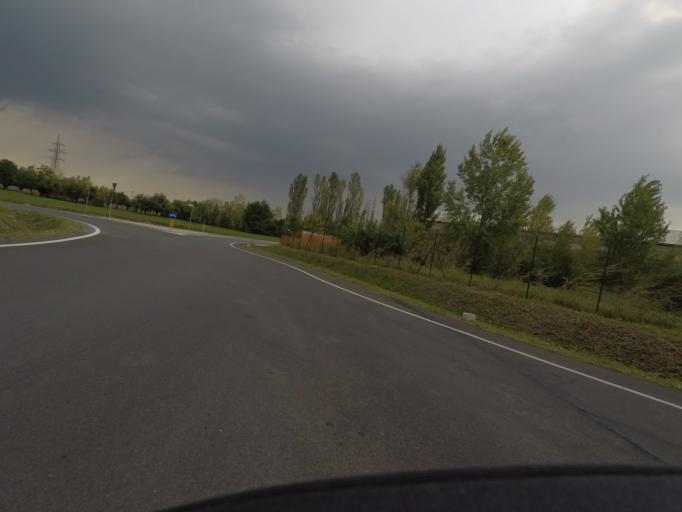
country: IT
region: Friuli Venezia Giulia
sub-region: Provincia di Udine
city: Feletto Umberto
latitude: 46.0976
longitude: 13.2415
